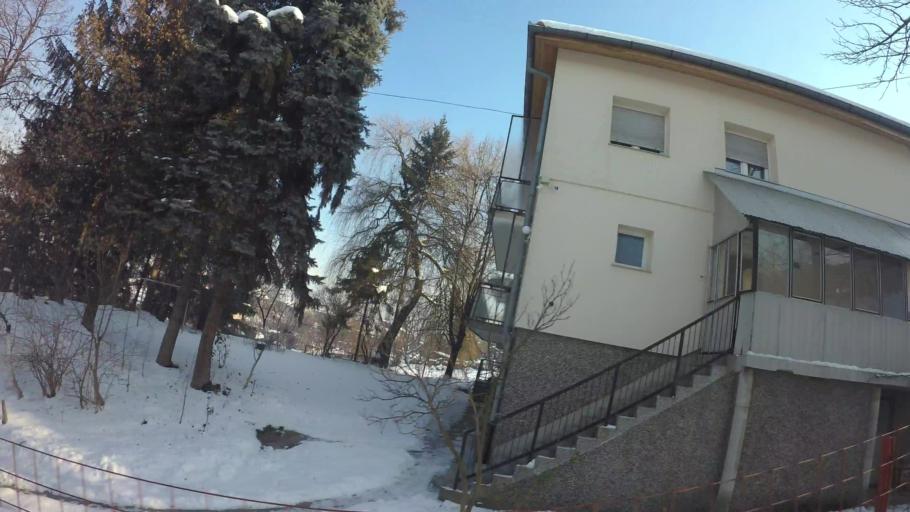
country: BA
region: Federation of Bosnia and Herzegovina
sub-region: Kanton Sarajevo
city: Sarajevo
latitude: 43.8416
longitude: 18.3579
